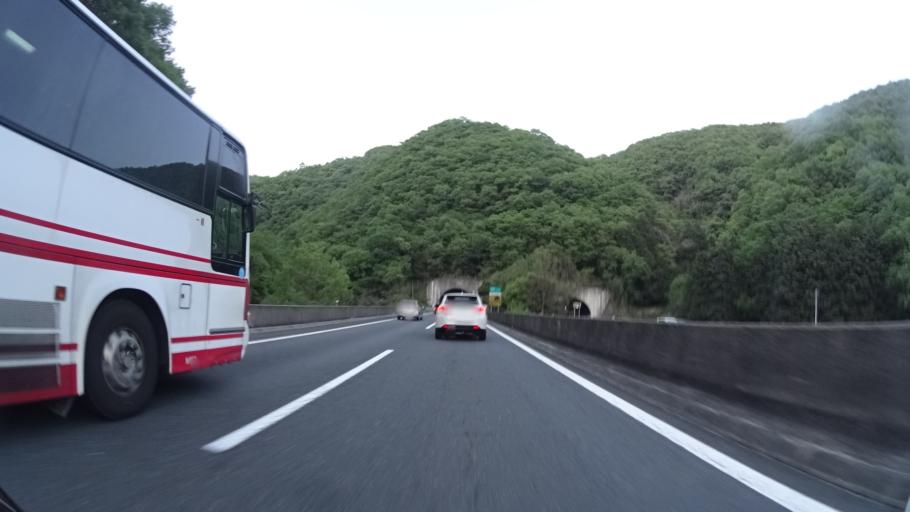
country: JP
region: Okayama
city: Okayama-shi
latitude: 34.7339
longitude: 133.9827
